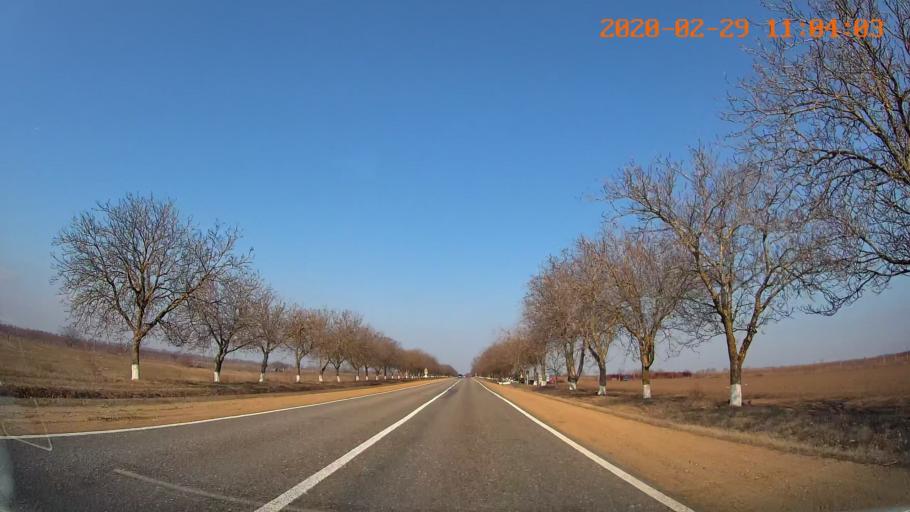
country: MD
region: Criuleni
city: Criuleni
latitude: 47.1841
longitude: 29.2069
